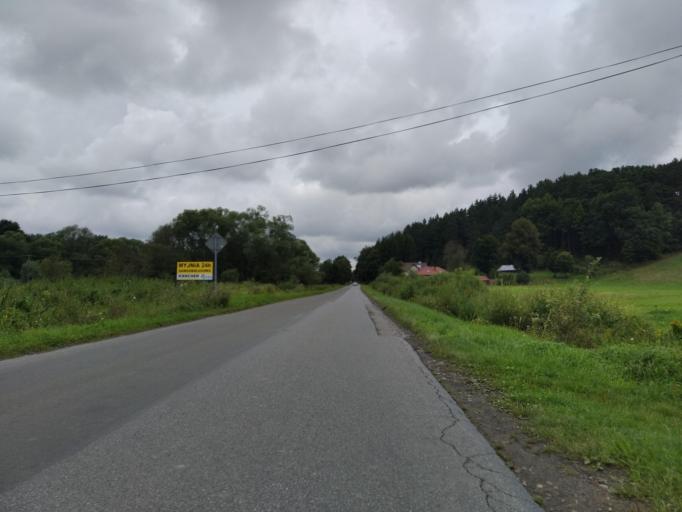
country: PL
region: Subcarpathian Voivodeship
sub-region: Powiat przemyski
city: Bircza
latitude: 49.6802
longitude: 22.4085
